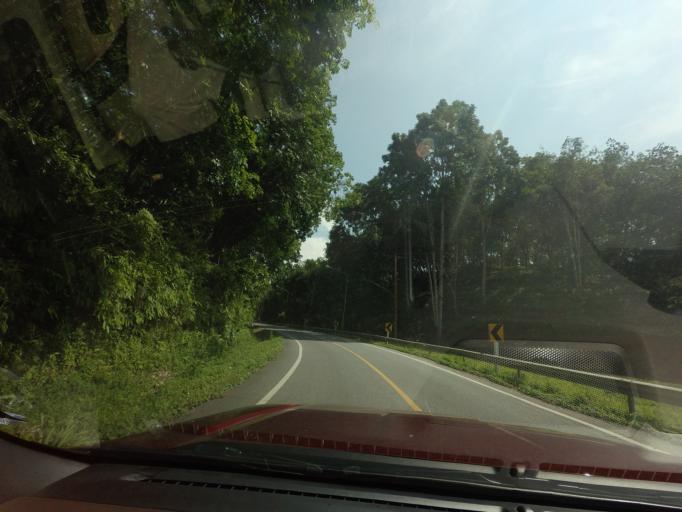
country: TH
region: Yala
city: Betong
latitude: 5.8333
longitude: 101.0795
